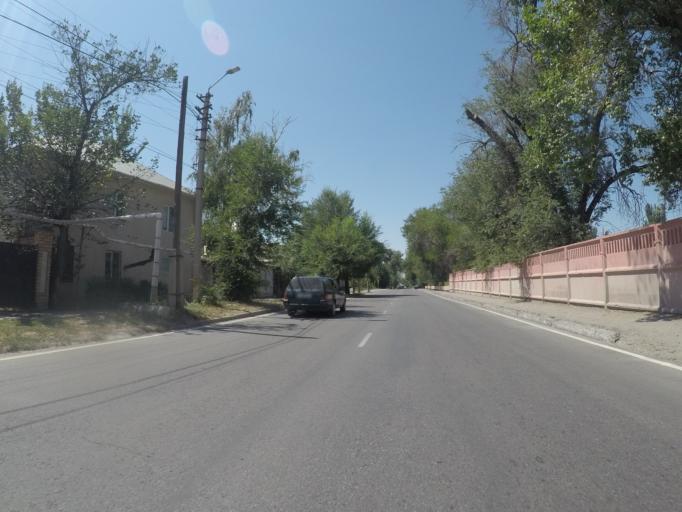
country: KG
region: Chuy
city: Bishkek
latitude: 42.8043
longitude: 74.5751
